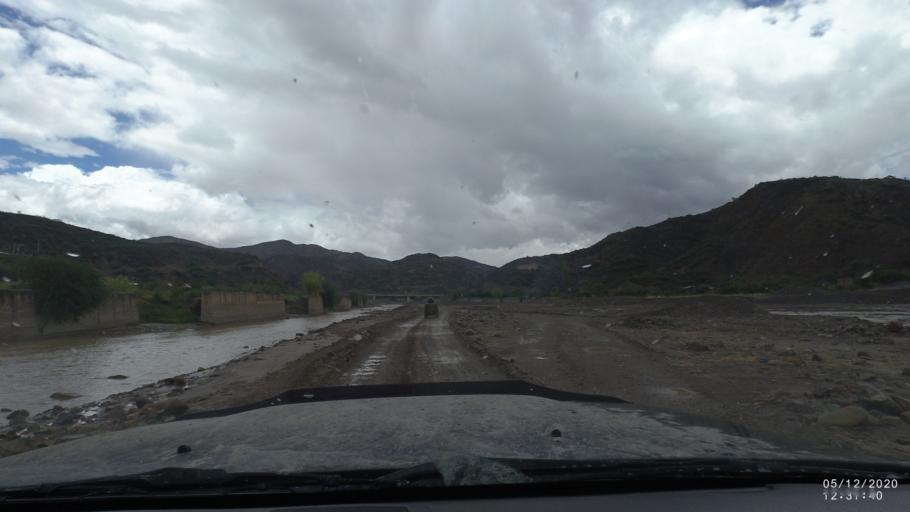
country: BO
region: Cochabamba
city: Sipe Sipe
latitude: -17.5448
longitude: -66.4206
